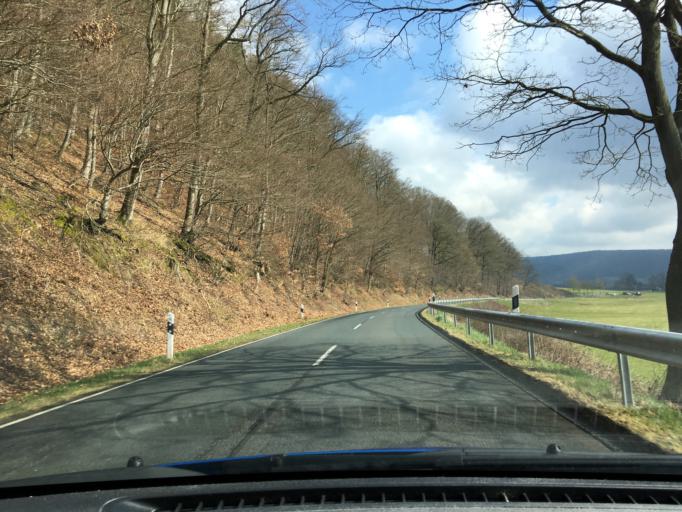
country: DE
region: Lower Saxony
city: Buhren
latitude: 51.5102
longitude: 9.5990
